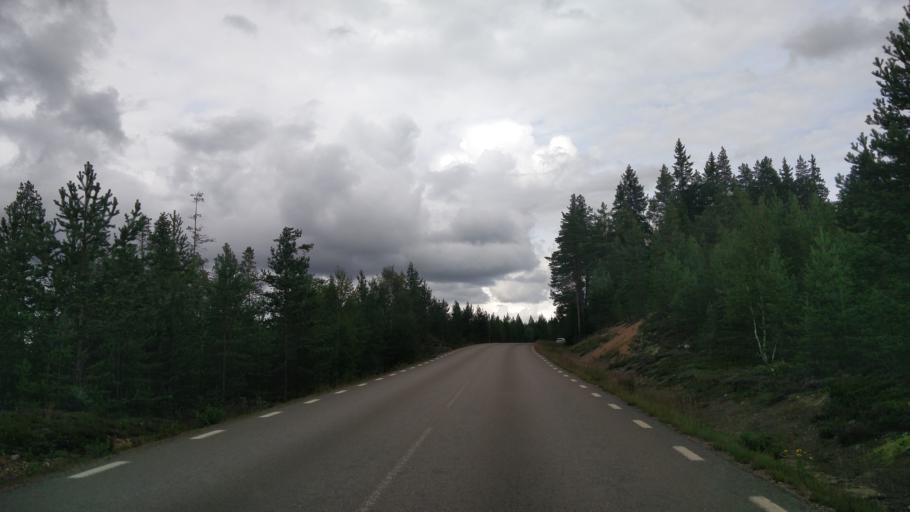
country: NO
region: Hedmark
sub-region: Trysil
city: Innbygda
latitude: 61.1574
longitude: 12.8159
